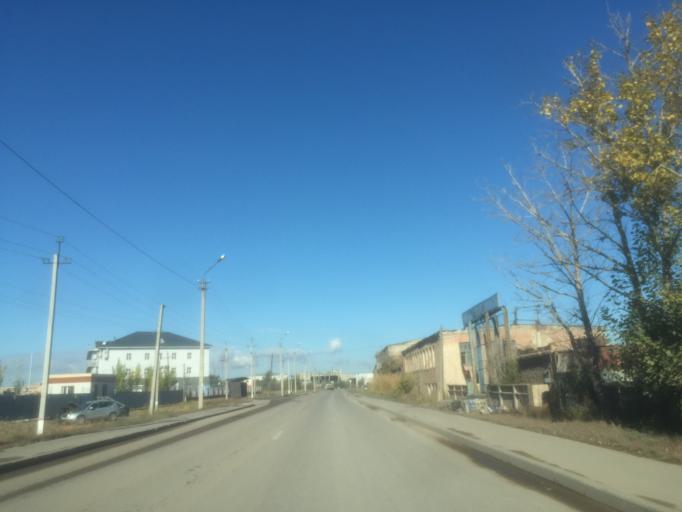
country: KZ
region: Astana Qalasy
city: Astana
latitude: 51.2078
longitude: 71.3556
